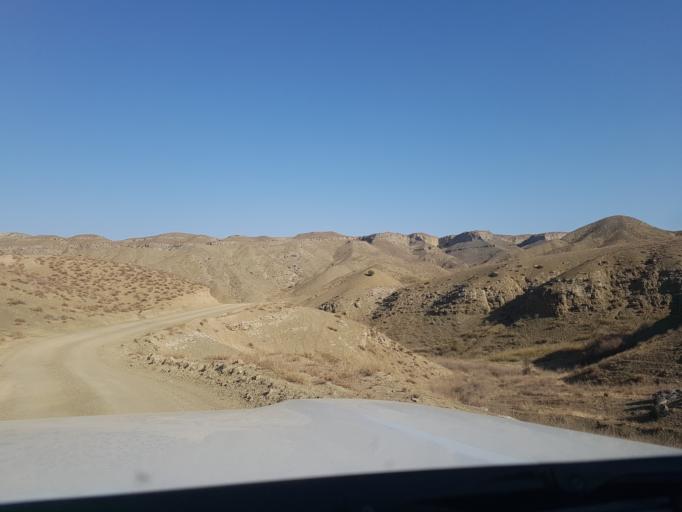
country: TM
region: Balkan
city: Magtymguly
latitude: 38.3011
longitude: 56.7758
